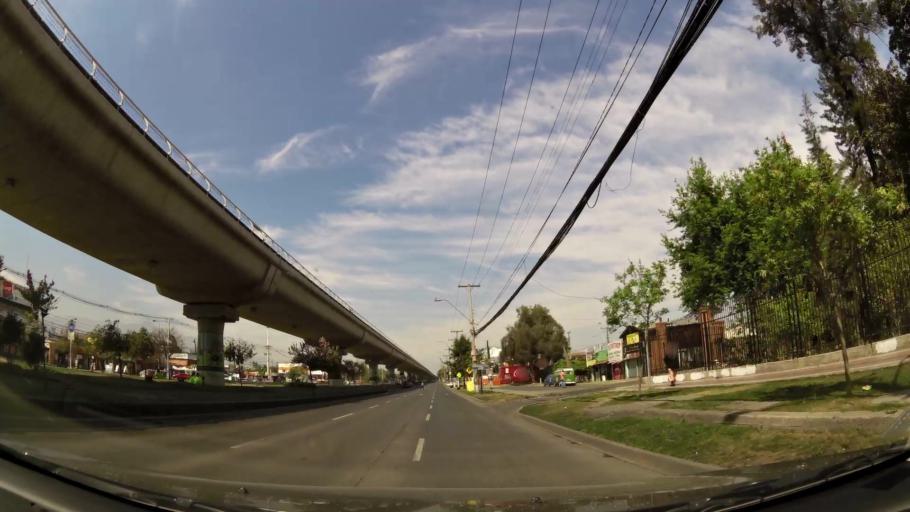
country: CL
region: Santiago Metropolitan
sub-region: Provincia de Cordillera
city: Puente Alto
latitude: -33.5805
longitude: -70.5817
